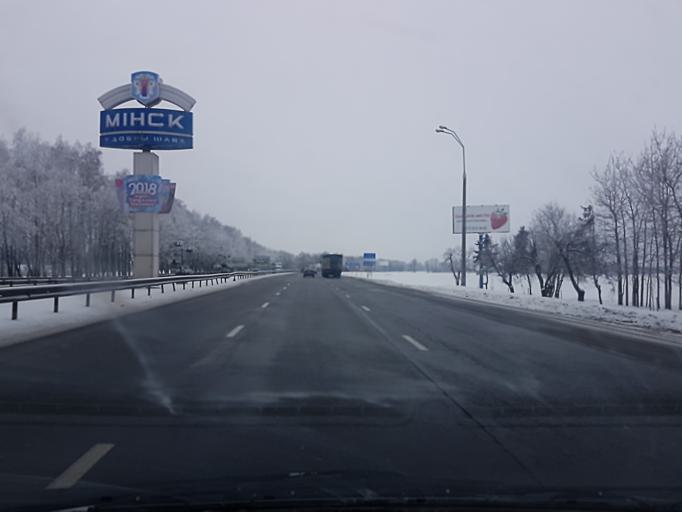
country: BY
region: Minsk
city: Shchomyslitsa
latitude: 53.8358
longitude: 27.4621
